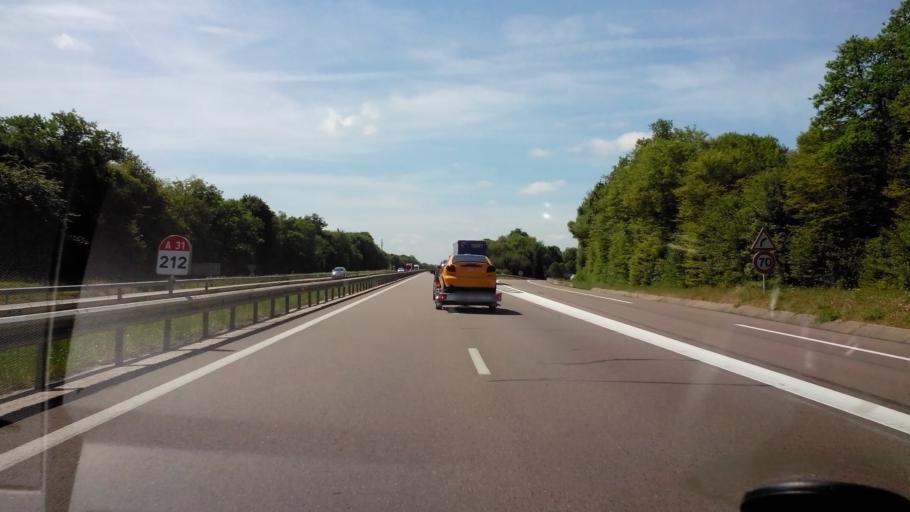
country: FR
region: Lorraine
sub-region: Departement de Meurthe-et-Moselle
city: Colombey-les-Belles
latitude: 48.5130
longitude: 5.9141
